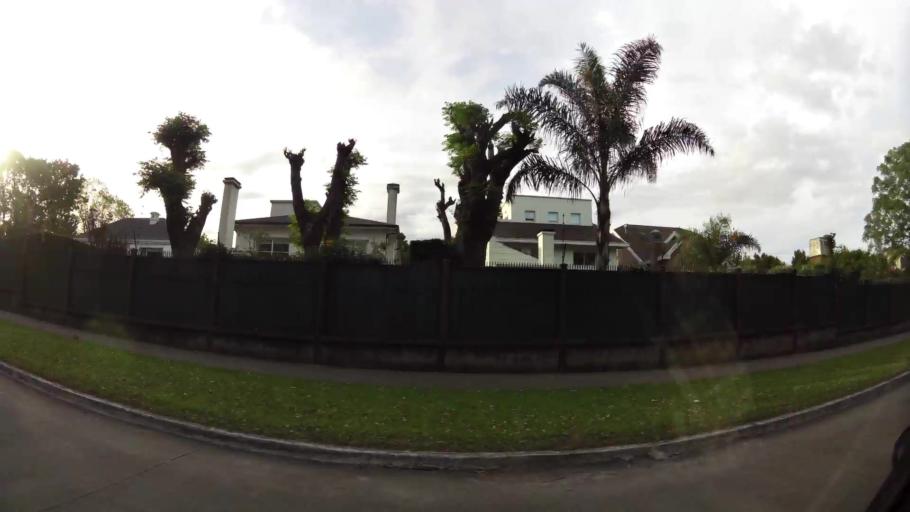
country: AR
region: Buenos Aires
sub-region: Partido de Quilmes
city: Quilmes
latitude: -34.7243
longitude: -58.2431
